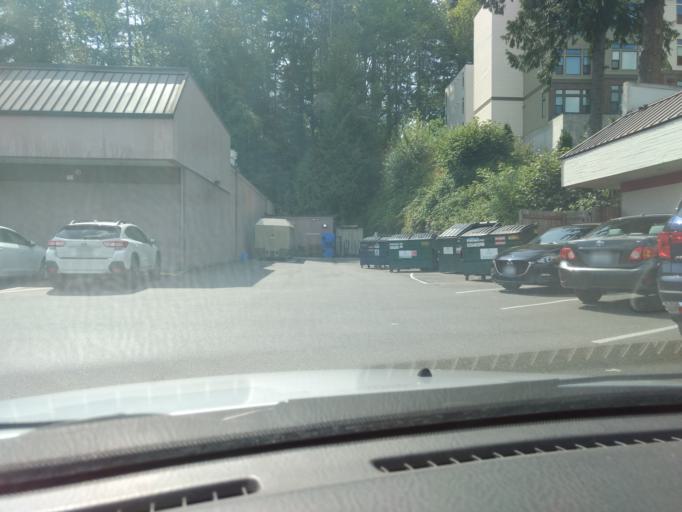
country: US
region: Washington
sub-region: King County
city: Bothell
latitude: 47.7656
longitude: -122.2111
